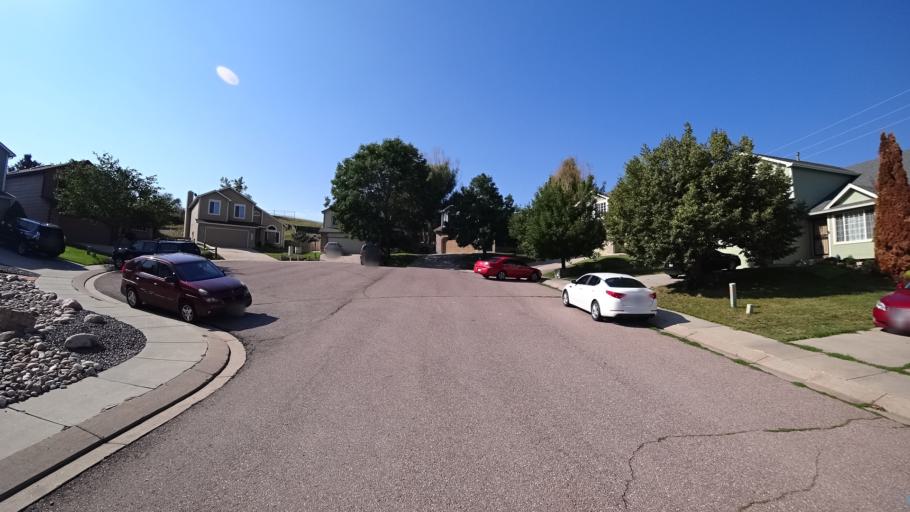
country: US
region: Colorado
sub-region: El Paso County
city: Air Force Academy
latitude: 38.9492
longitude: -104.7837
